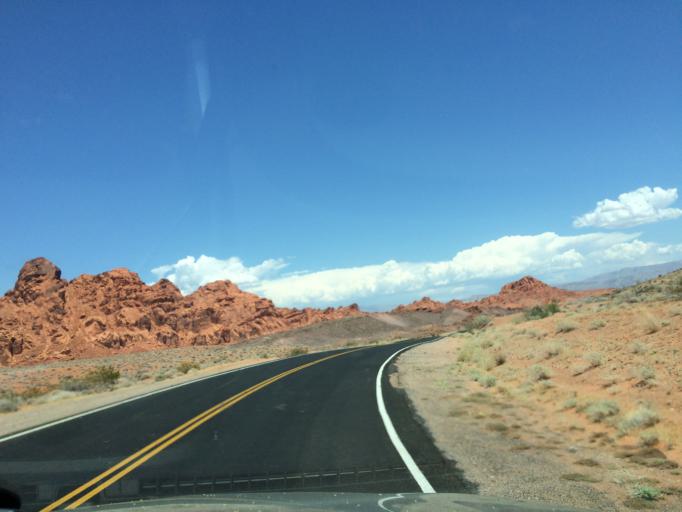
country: US
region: Nevada
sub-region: Clark County
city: Moapa Valley
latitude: 36.4270
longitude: -114.4816
